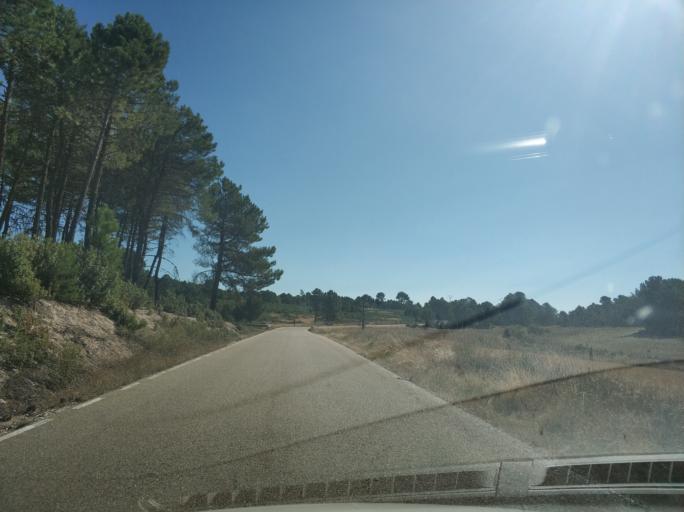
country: ES
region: Castille and Leon
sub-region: Provincia de Soria
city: Santa Maria de las Hoyas
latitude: 41.7785
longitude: -3.1847
